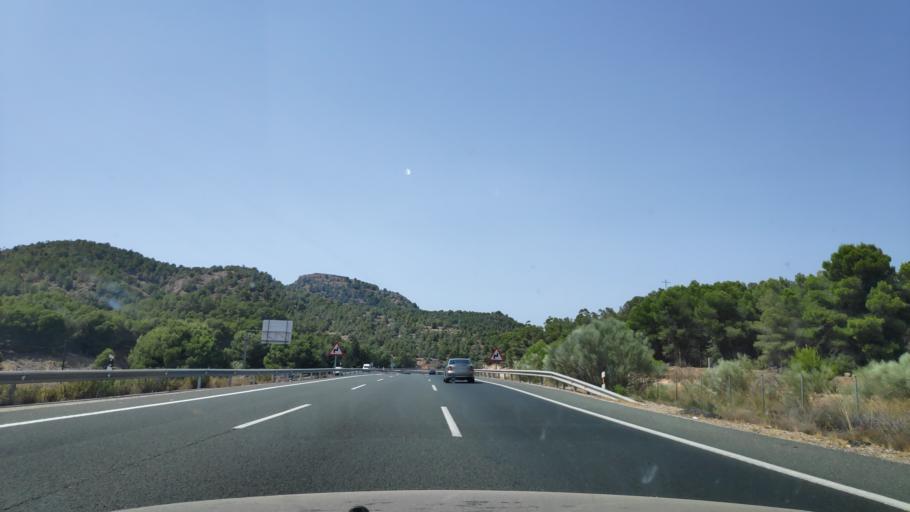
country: ES
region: Murcia
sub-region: Murcia
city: Murcia
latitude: 37.8898
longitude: -1.1409
